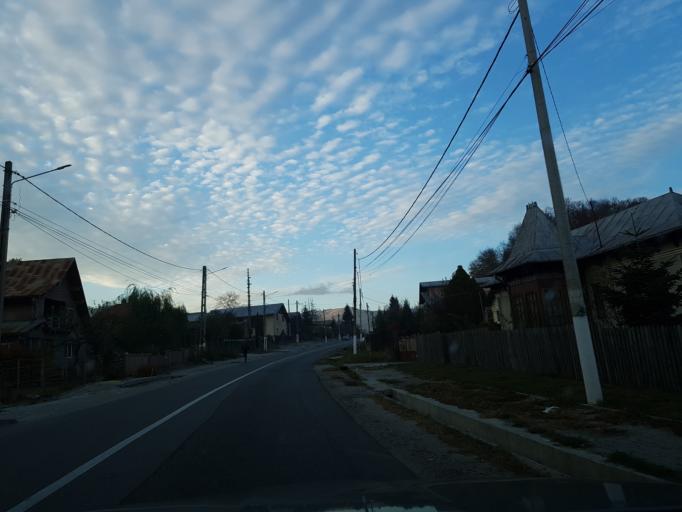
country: RO
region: Prahova
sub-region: Oras Breaza
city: Gura Beliei
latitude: 45.2104
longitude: 25.6469
